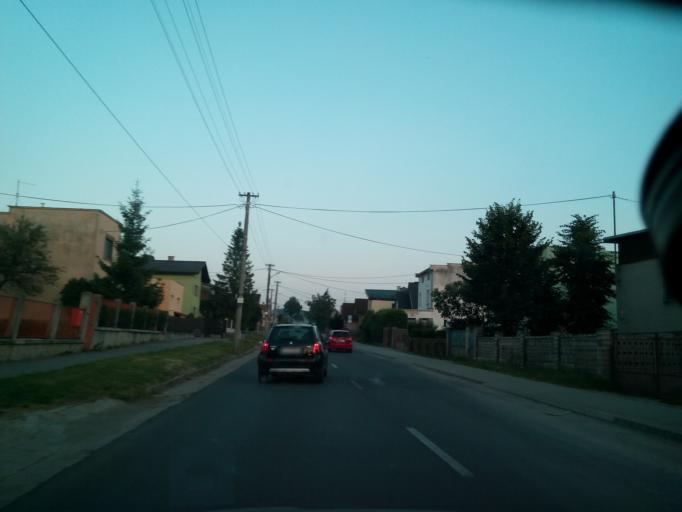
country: SK
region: Presovsky
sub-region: Okres Presov
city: Kezmarok
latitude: 49.1311
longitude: 20.4345
